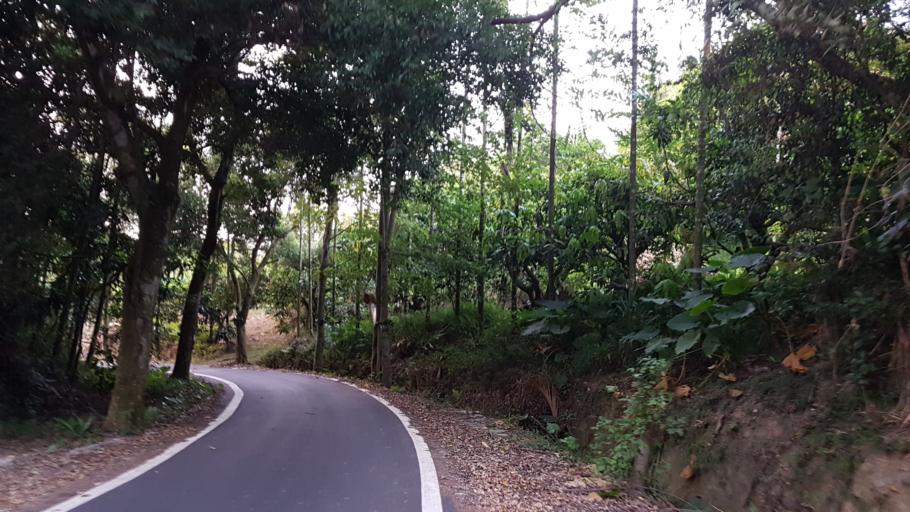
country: TW
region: Taiwan
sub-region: Chiayi
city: Jiayi Shi
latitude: 23.3633
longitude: 120.4656
